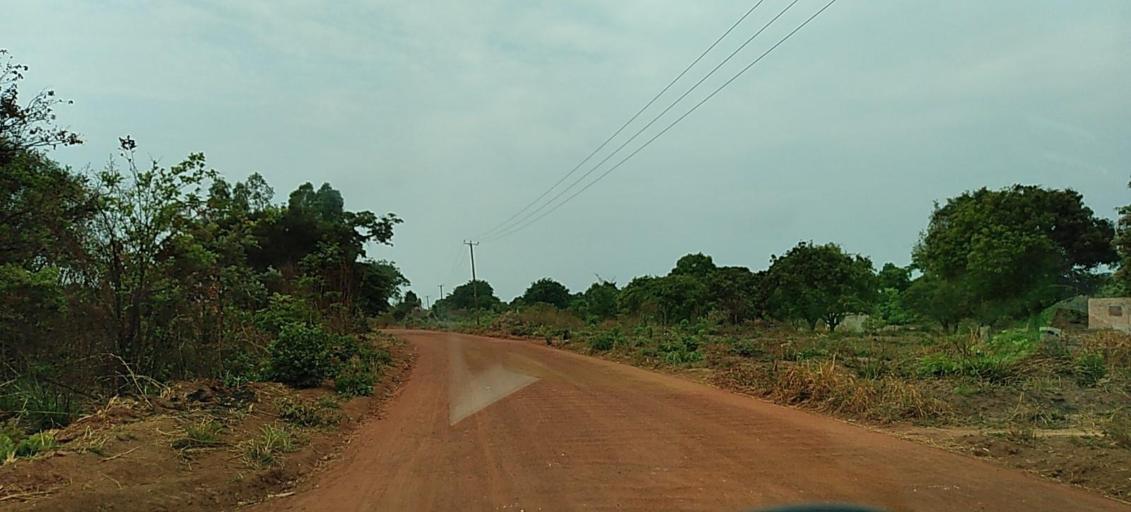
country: ZM
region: North-Western
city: Solwezi
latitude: -12.2376
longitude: 26.5112
